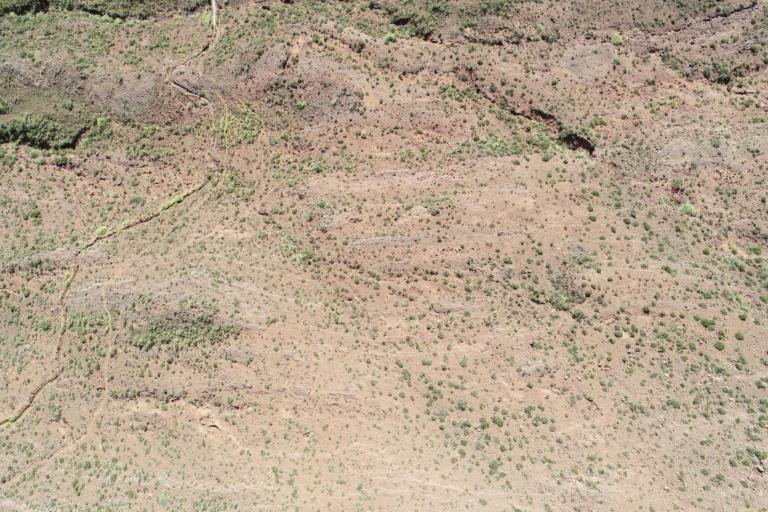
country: BO
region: La Paz
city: Tiahuanaco
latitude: -16.6064
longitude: -68.7571
